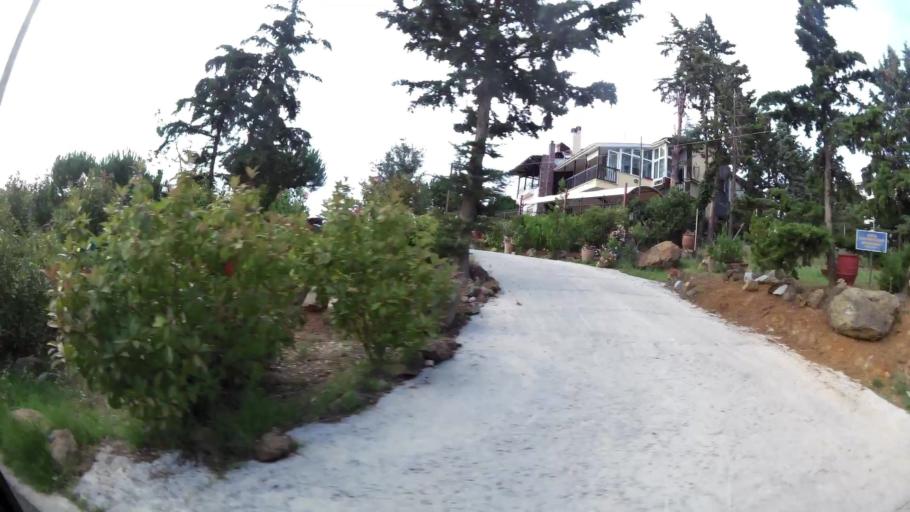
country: GR
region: Central Macedonia
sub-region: Nomos Thessalonikis
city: Pefka
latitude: 40.6602
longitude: 22.9953
